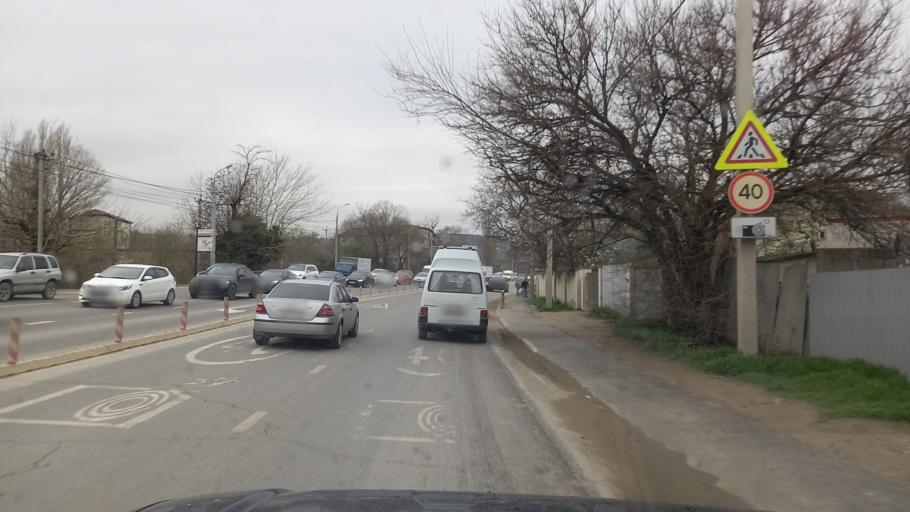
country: RU
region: Krasnodarskiy
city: Gayduk
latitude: 44.7683
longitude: 37.7020
